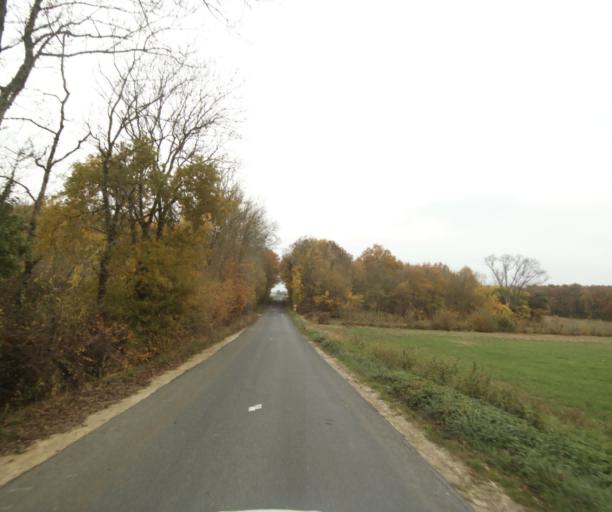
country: FR
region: Poitou-Charentes
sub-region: Departement de la Charente-Maritime
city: Chermignac
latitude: 45.7103
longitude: -0.6925
